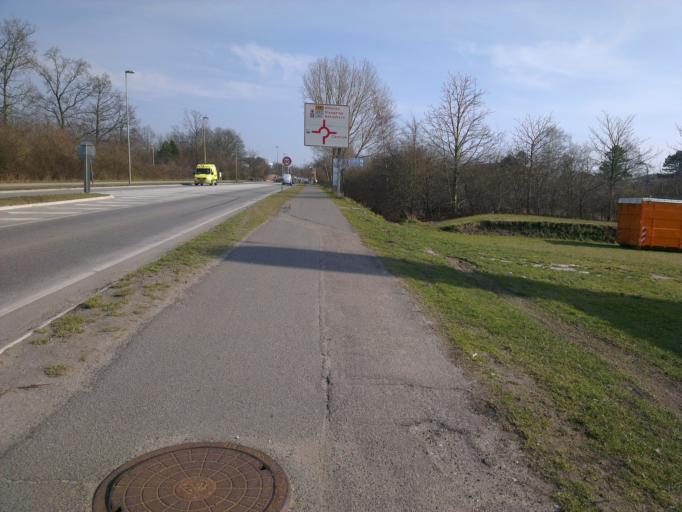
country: DK
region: Capital Region
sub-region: Frederikssund Kommune
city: Frederikssund
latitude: 55.8446
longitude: 12.0613
